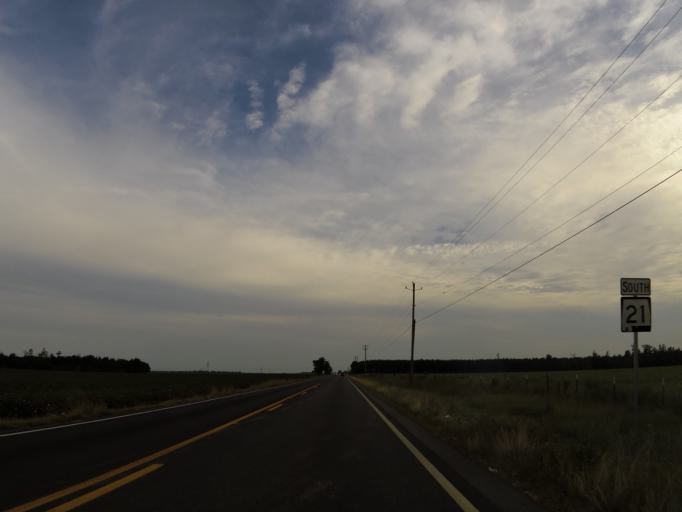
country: US
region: Alabama
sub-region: Escambia County
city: Atmore
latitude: 31.1792
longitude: -87.4637
